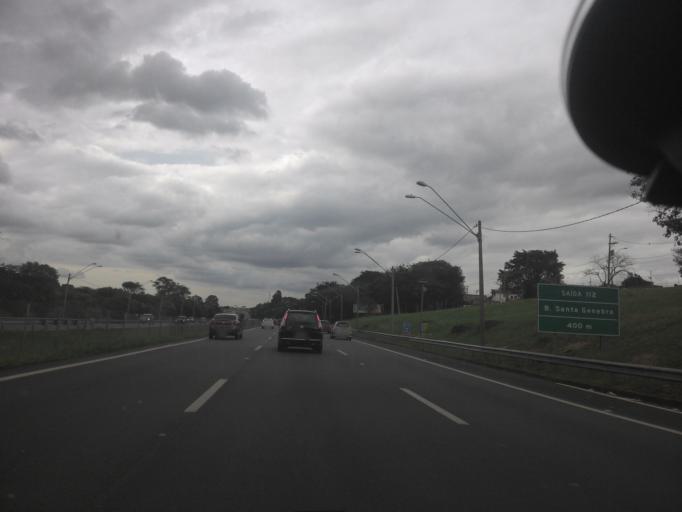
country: BR
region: Sao Paulo
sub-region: Campinas
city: Campinas
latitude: -22.8587
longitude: -47.0723
